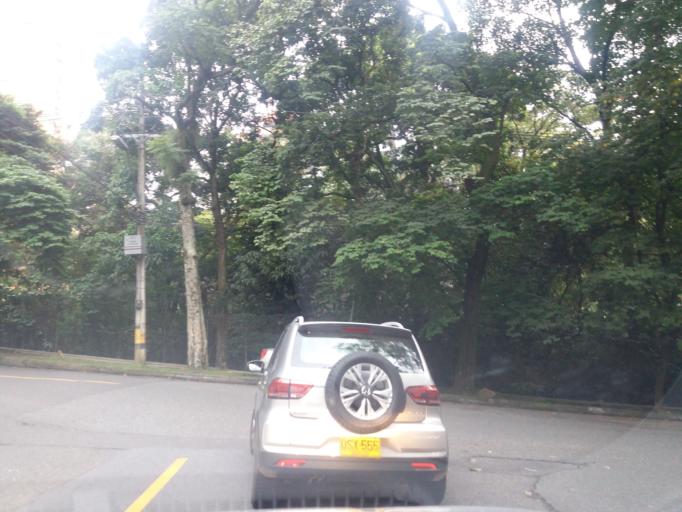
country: CO
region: Antioquia
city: Itagui
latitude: 6.2046
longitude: -75.5690
